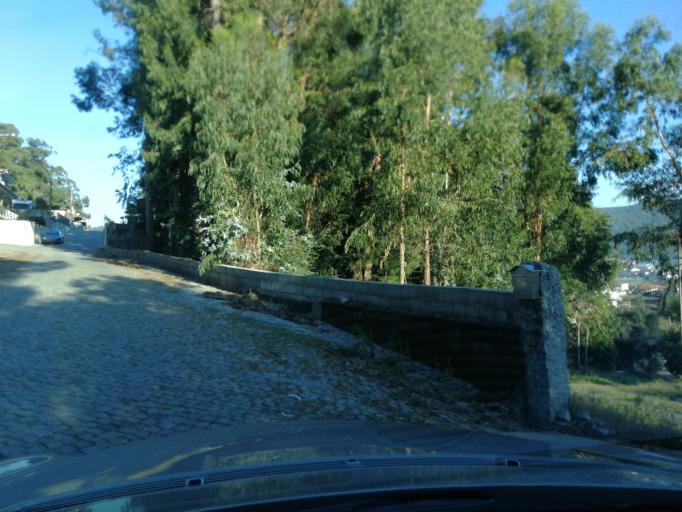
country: PT
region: Braga
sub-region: Braga
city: Oliveira
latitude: 41.4540
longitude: -8.4630
